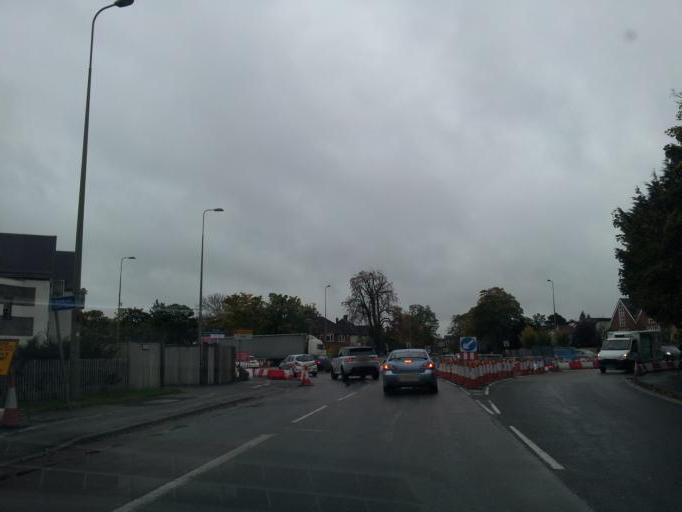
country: GB
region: England
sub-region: Oxfordshire
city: Kidlington
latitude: 51.7888
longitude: -1.2706
